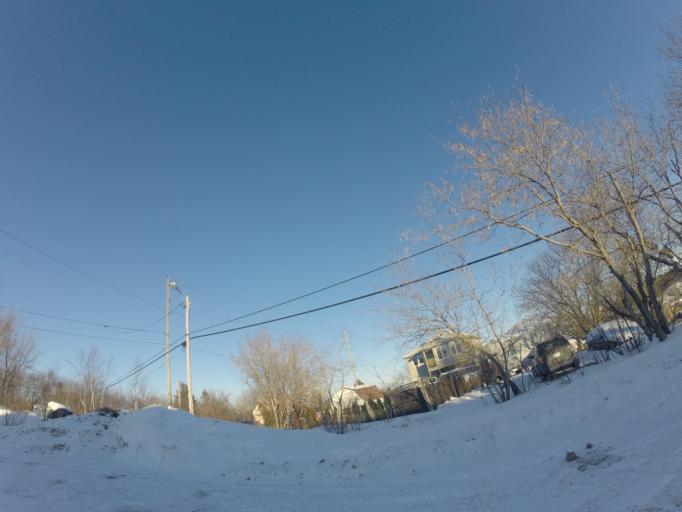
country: CA
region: Ontario
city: Greater Sudbury
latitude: 46.5040
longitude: -81.0015
